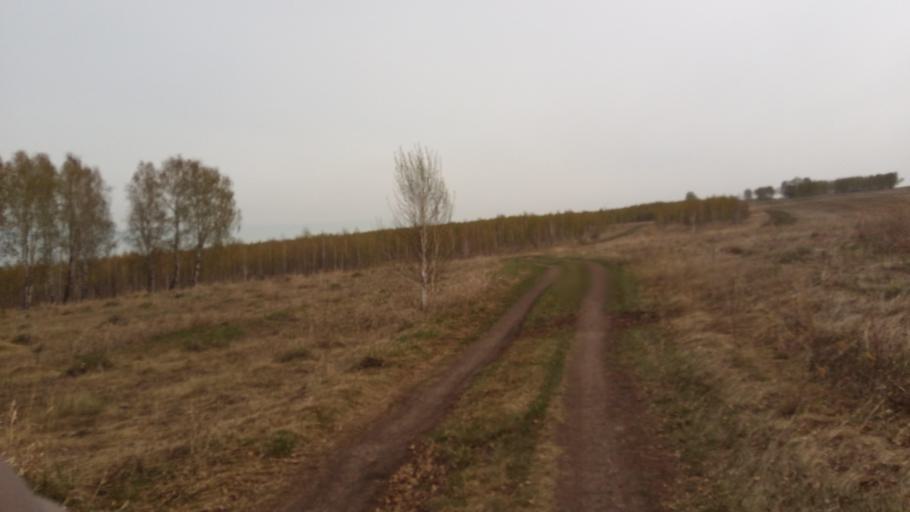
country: RU
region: Chelyabinsk
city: Timiryazevskiy
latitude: 55.0069
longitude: 60.8622
